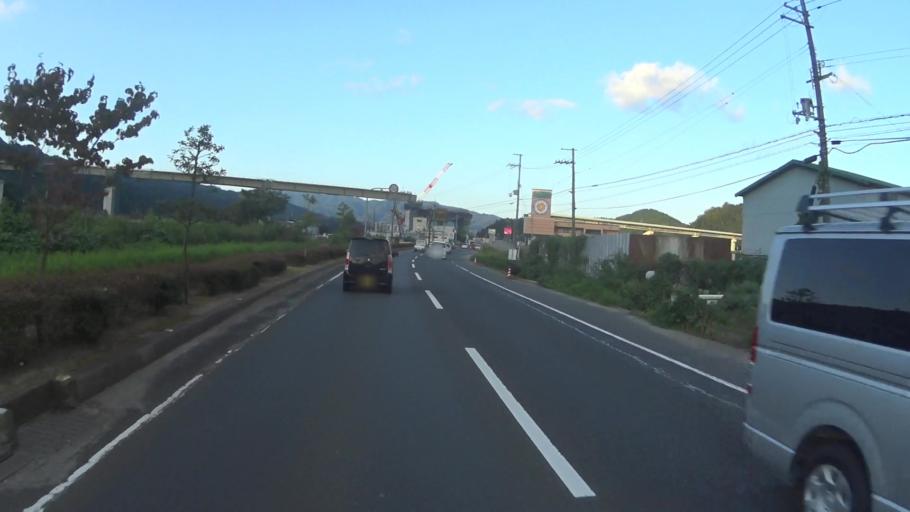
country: JP
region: Kyoto
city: Miyazu
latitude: 35.5491
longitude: 135.1371
